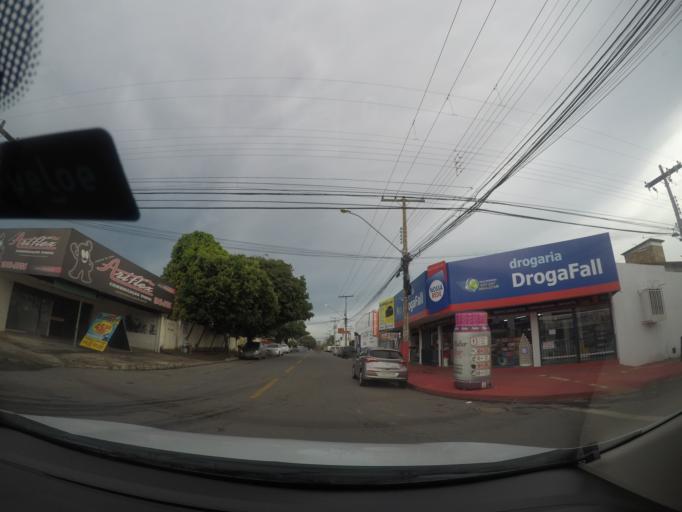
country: BR
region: Goias
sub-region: Goiania
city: Goiania
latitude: -16.7032
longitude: -49.3075
